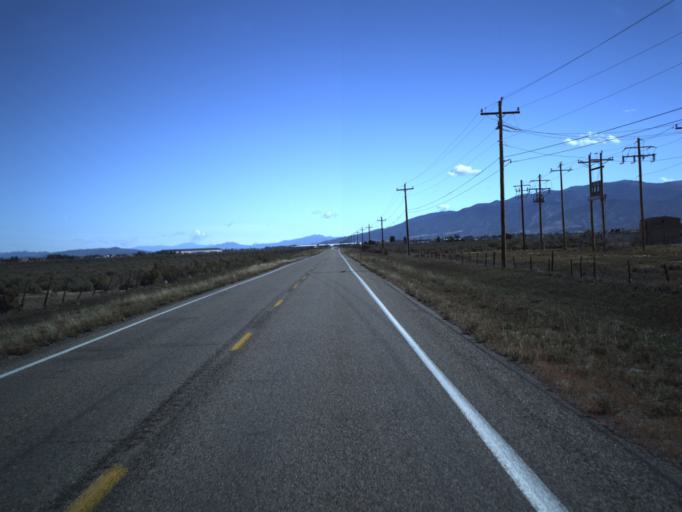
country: US
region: Utah
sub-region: Iron County
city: Cedar City
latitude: 37.6688
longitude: -113.1953
